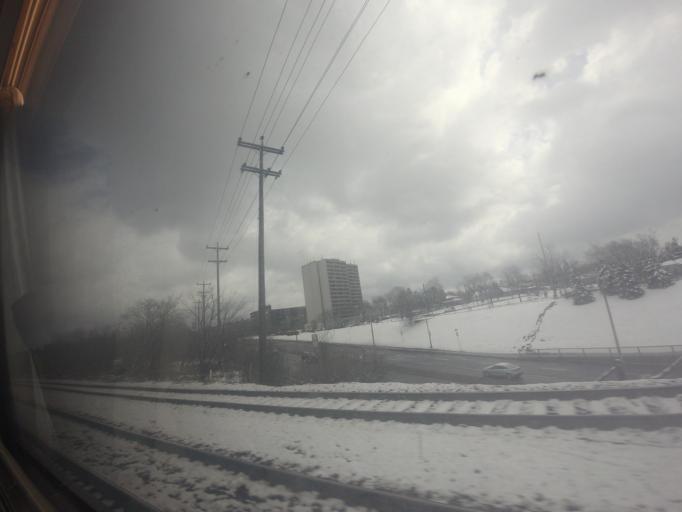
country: CA
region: Ontario
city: Scarborough
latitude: 43.7412
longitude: -79.2298
